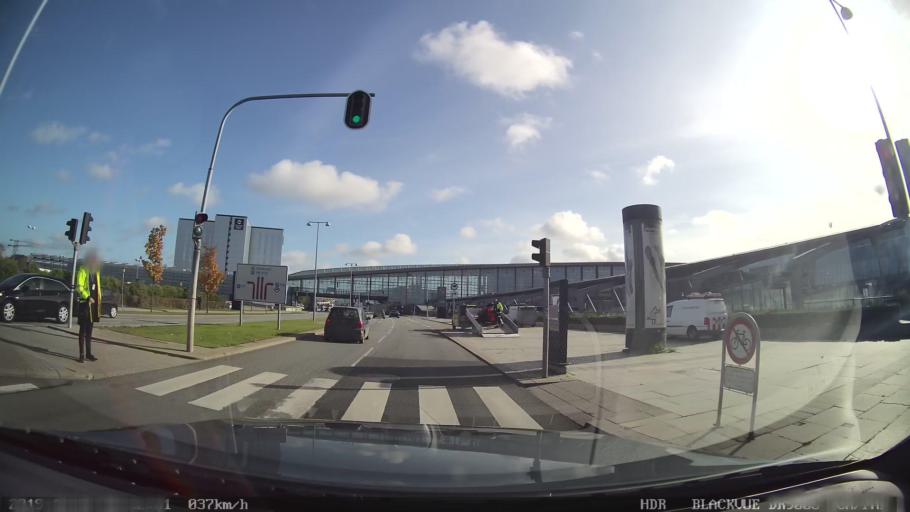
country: DK
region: Capital Region
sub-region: Dragor Kommune
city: Dragor
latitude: 55.6298
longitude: 12.6459
